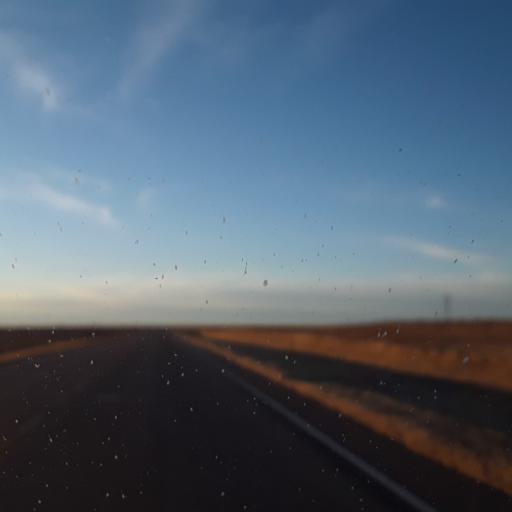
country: US
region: Colorado
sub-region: Cheyenne County
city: Cheyenne Wells
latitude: 38.8136
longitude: -102.4741
